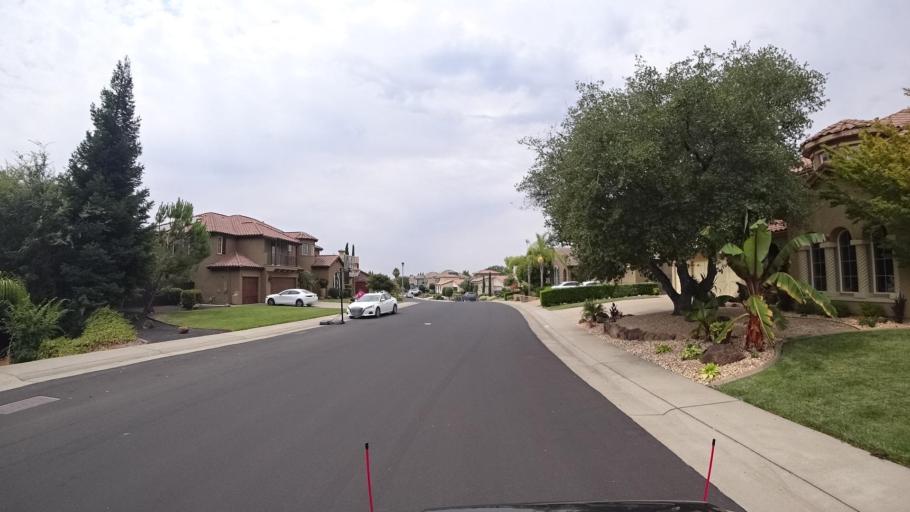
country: US
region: California
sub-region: Placer County
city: Rocklin
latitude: 38.7760
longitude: -121.2219
